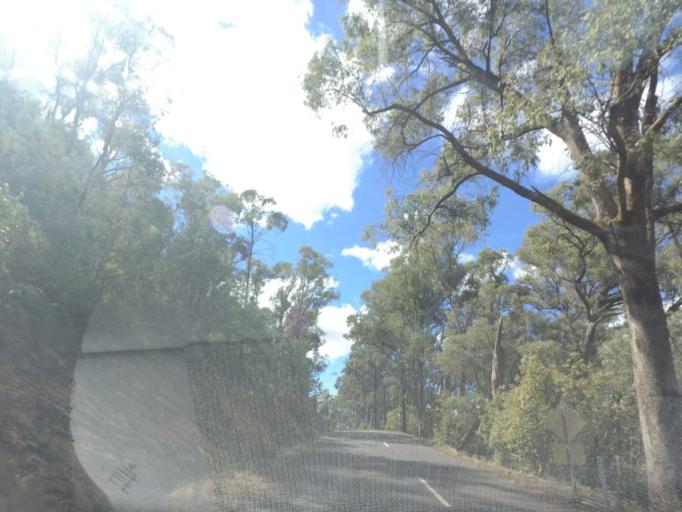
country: AU
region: Victoria
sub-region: Murrindindi
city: Alexandra
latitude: -37.3301
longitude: 145.9424
